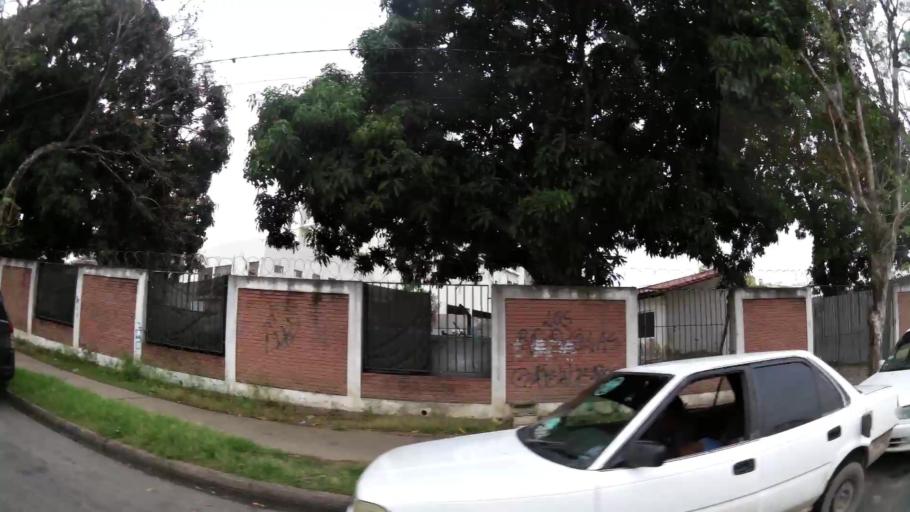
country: BO
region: Santa Cruz
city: Santa Cruz de la Sierra
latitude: -17.7768
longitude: -63.1870
